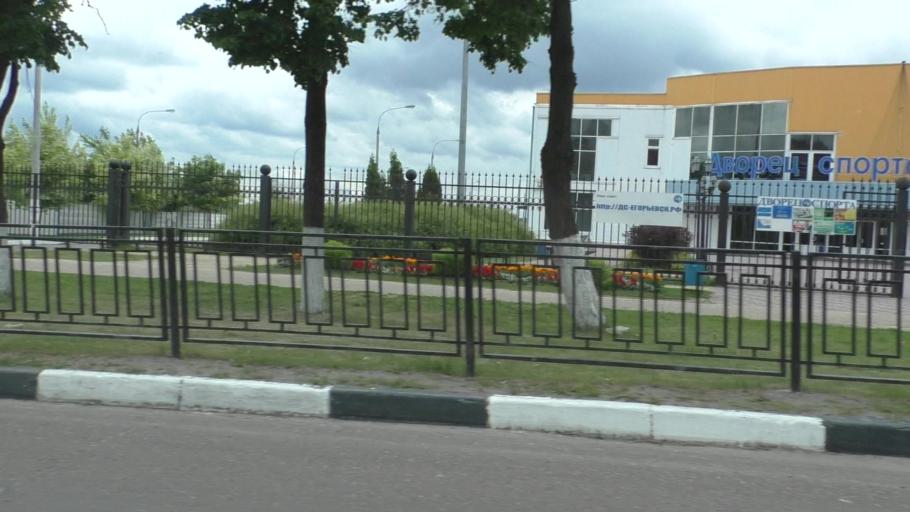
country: RU
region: Moskovskaya
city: Yegor'yevsk
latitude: 55.3745
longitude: 39.0491
